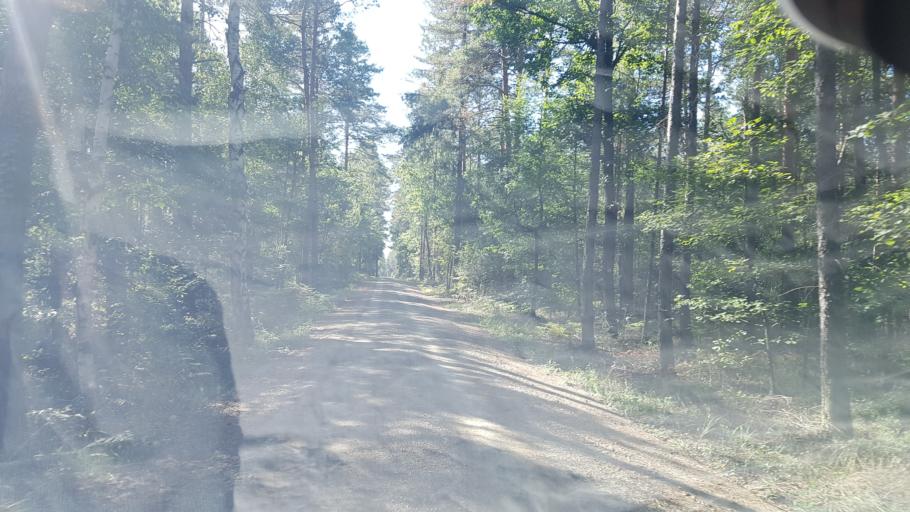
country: DE
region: Brandenburg
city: Ruckersdorf
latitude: 51.5412
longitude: 13.5813
